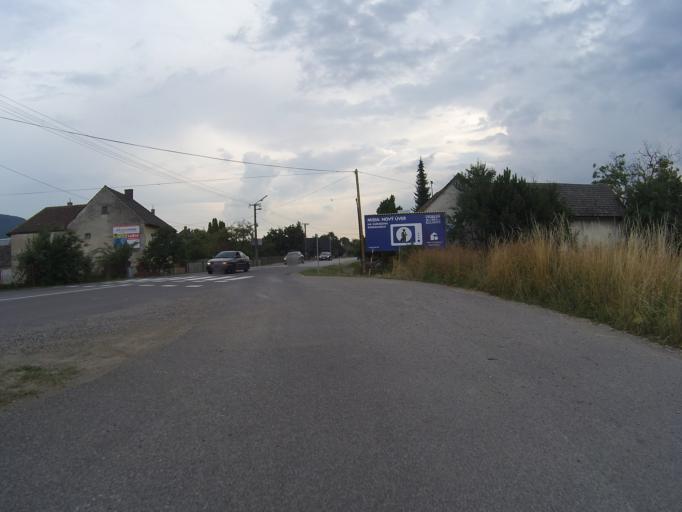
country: SK
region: Nitriansky
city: Ilava
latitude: 49.0439
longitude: 18.2955
